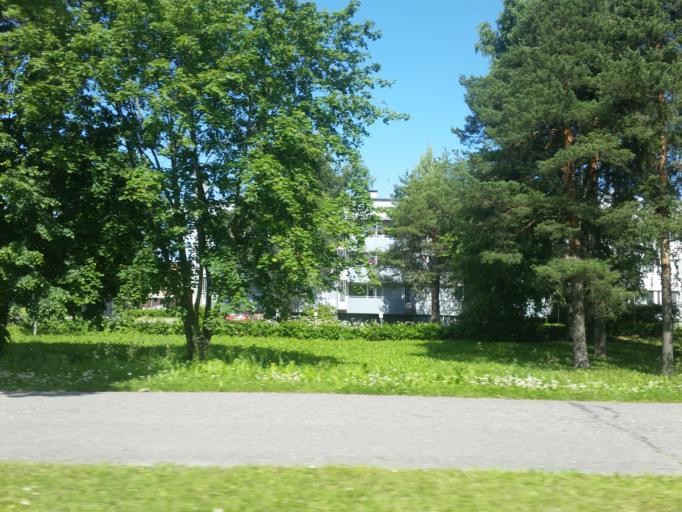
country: FI
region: Northern Savo
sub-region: Varkaus
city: Varkaus
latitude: 62.3122
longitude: 27.8774
